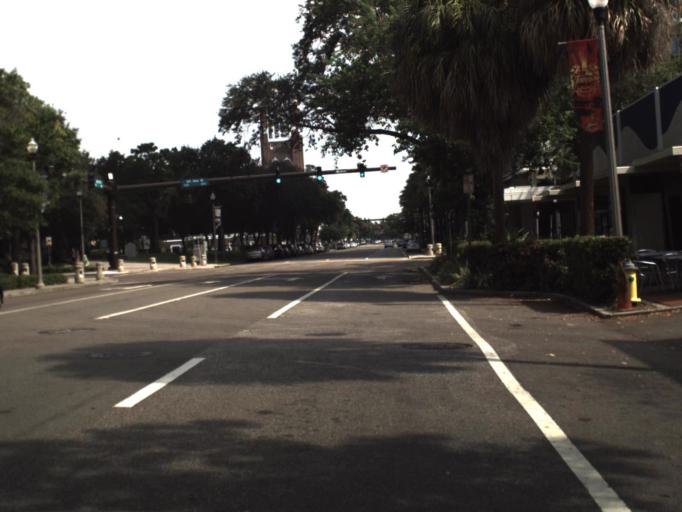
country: US
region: Florida
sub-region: Pinellas County
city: Saint Petersburg
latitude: 27.7715
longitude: -82.6370
